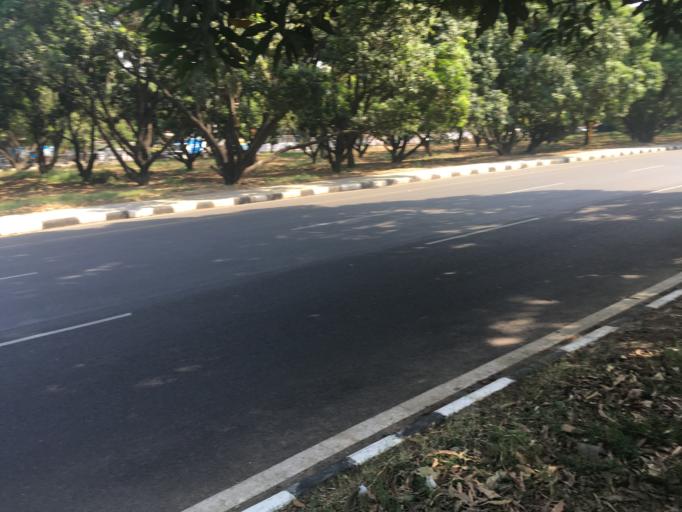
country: IN
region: Chandigarh
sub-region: Chandigarh
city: Chandigarh
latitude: 30.7093
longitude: 76.7986
